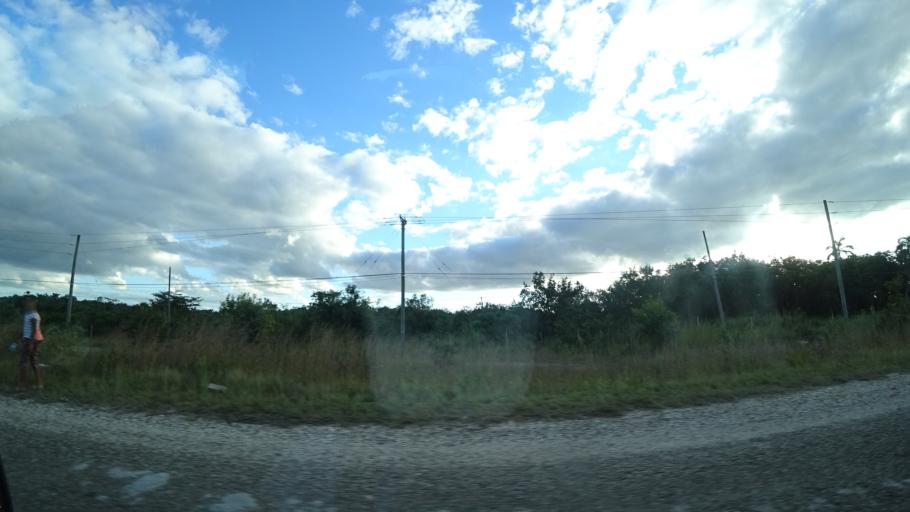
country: BZ
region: Belize
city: Belize City
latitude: 17.5796
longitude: -88.3713
